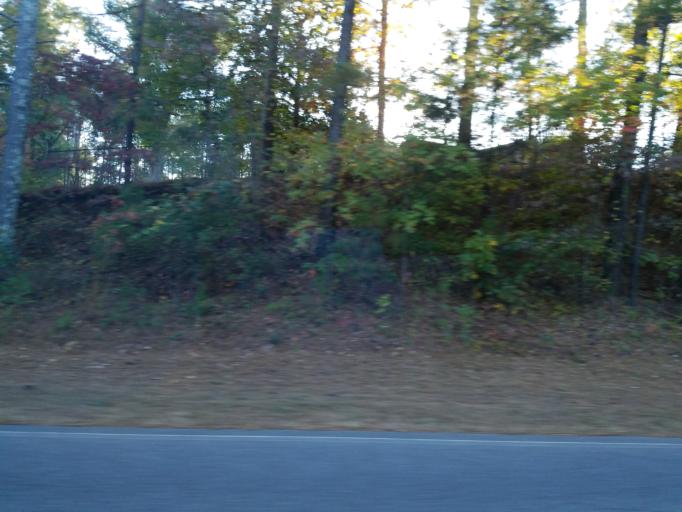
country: US
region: Georgia
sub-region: Bartow County
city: Euharlee
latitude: 34.2437
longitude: -84.9561
